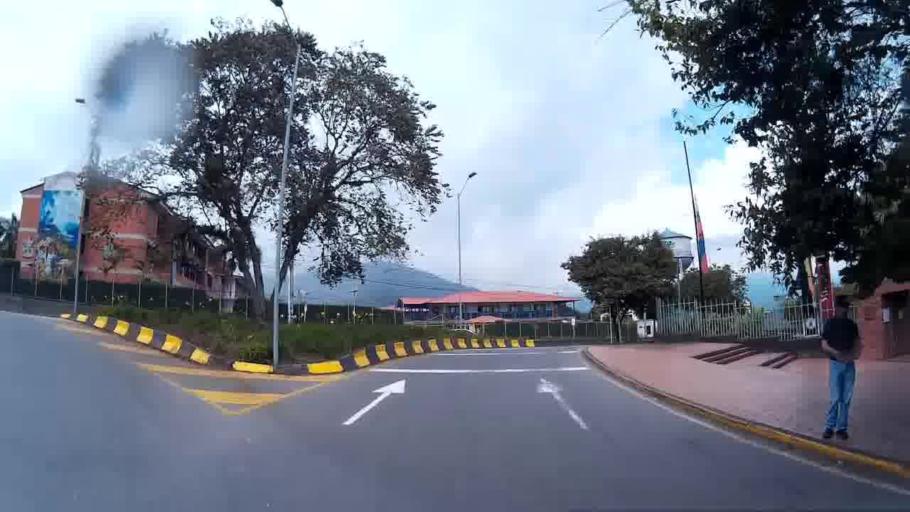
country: CO
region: Quindio
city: Calarca
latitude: 4.5715
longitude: -75.6479
